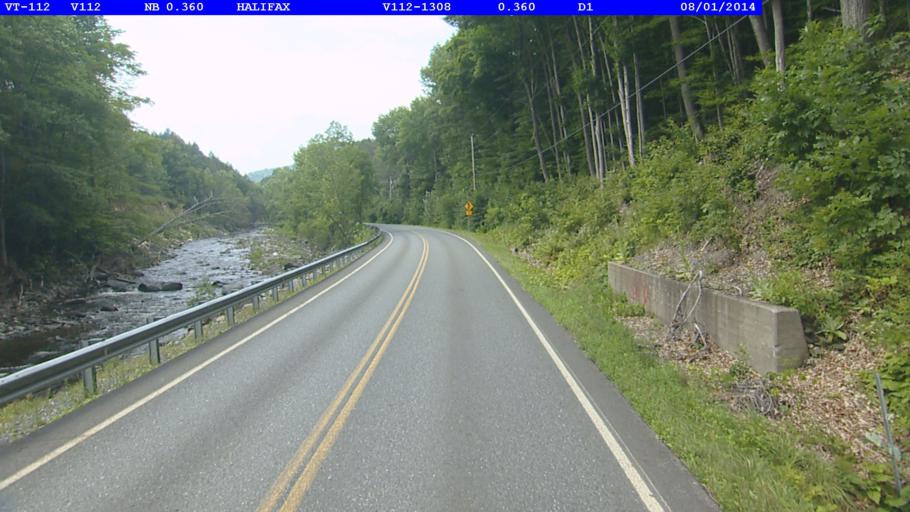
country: US
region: Massachusetts
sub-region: Franklin County
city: Colrain
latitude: 42.7384
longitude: -72.7254
